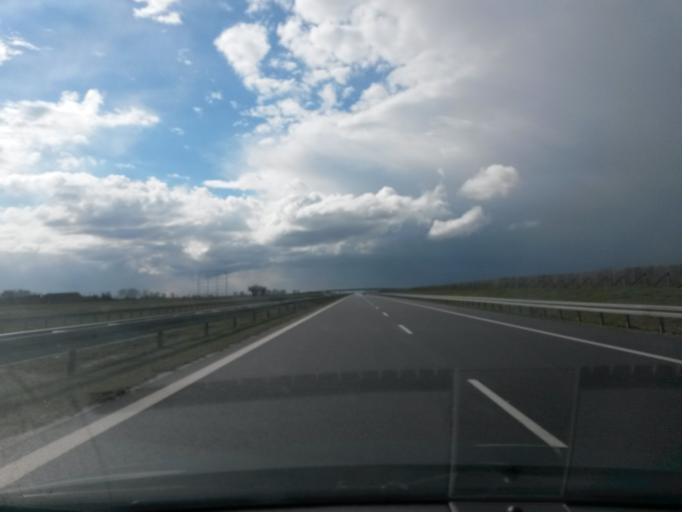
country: PL
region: Greater Poland Voivodeship
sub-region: Powiat wrzesinski
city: Nekla
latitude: 52.3185
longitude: 17.4792
